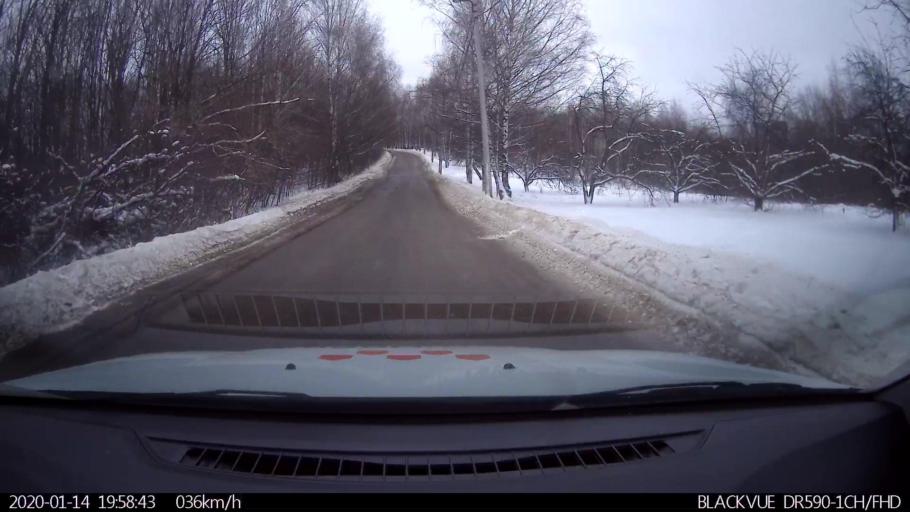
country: RU
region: Nizjnij Novgorod
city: Nizhniy Novgorod
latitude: 56.2386
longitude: 43.9413
